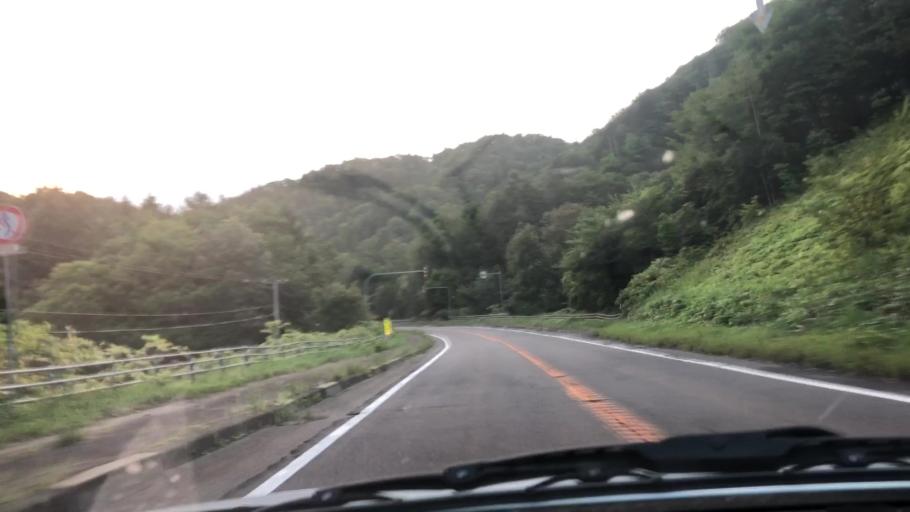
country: JP
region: Hokkaido
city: Chitose
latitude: 42.8724
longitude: 142.1425
